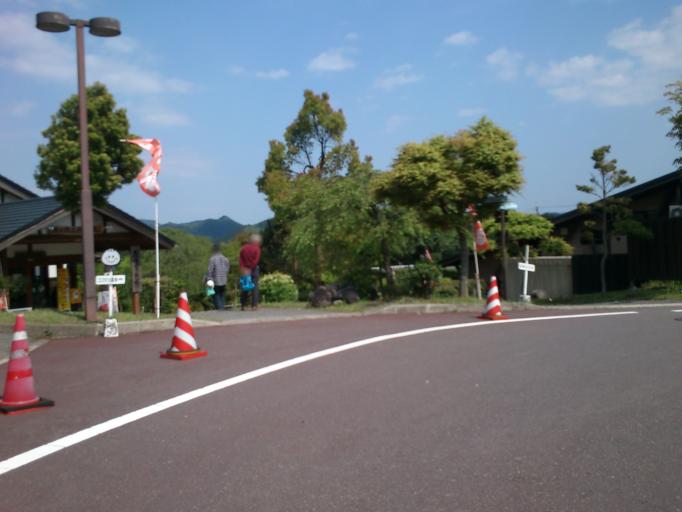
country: JP
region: Kyoto
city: Fukuchiyama
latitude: 35.3386
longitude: 134.9299
